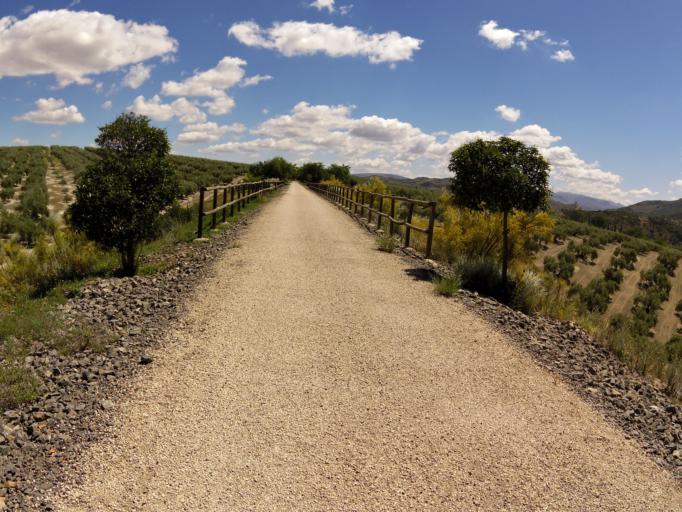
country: ES
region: Andalusia
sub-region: Provincia de Jaen
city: Alcaudete
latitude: 37.6484
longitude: -4.0667
